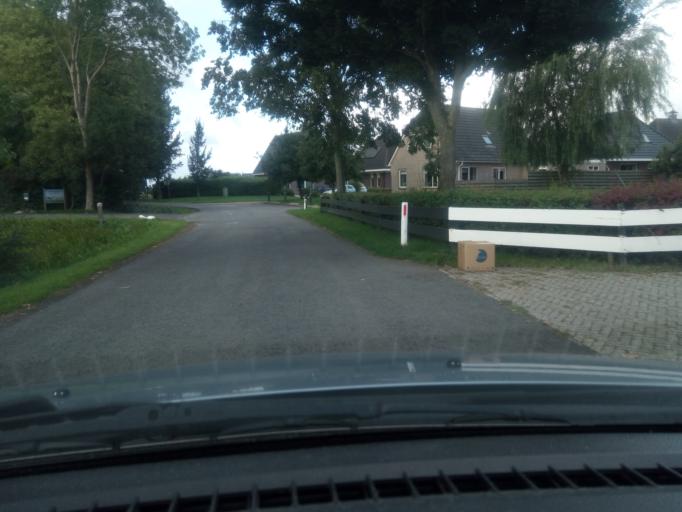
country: NL
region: Groningen
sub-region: Gemeente Grootegast
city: Grootegast
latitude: 53.2640
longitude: 6.2492
